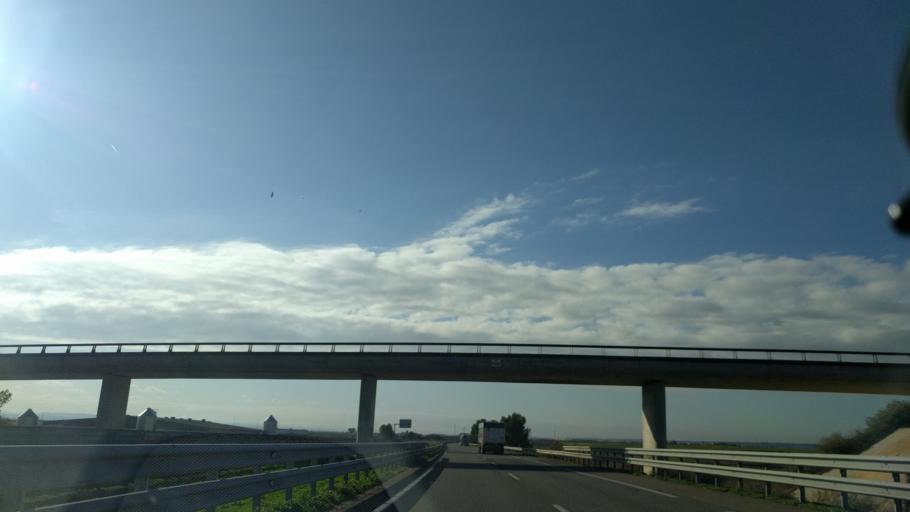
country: ES
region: Catalonia
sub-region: Provincia de Lleida
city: Alcarras
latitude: 41.5720
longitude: 0.5047
